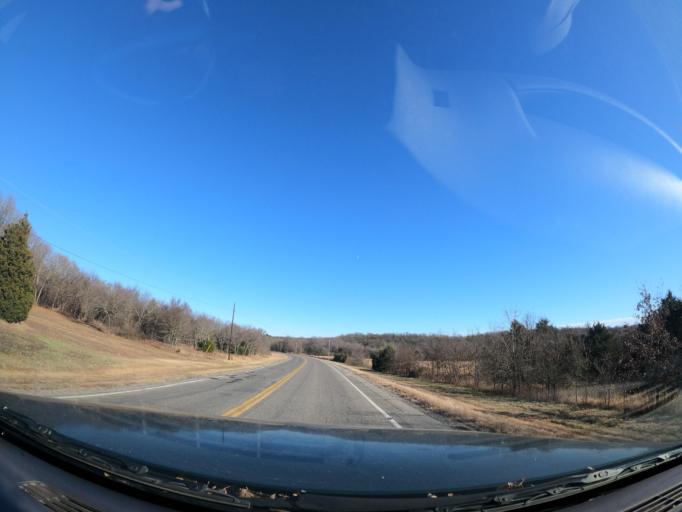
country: US
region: Oklahoma
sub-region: Pittsburg County
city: Longtown
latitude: 35.2144
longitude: -95.4191
